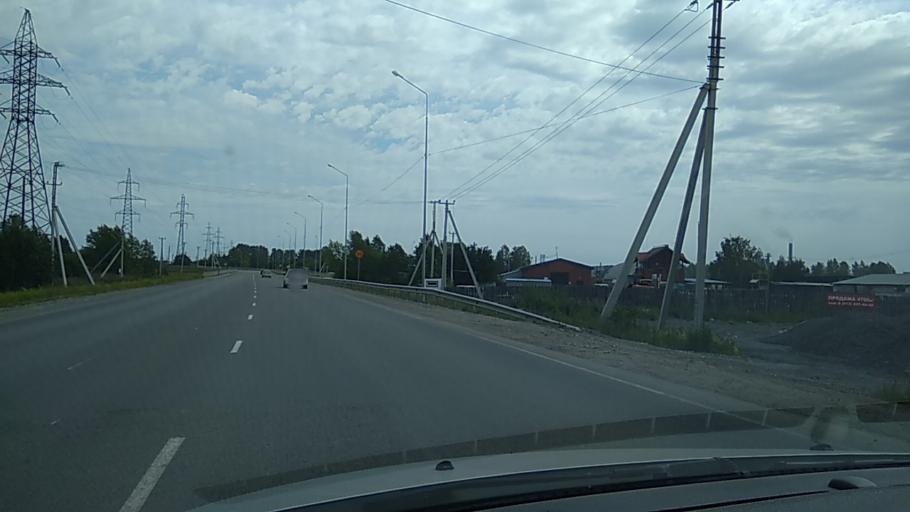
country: RU
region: Sverdlovsk
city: Verkhnyaya Pyshma
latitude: 56.9480
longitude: 60.5979
